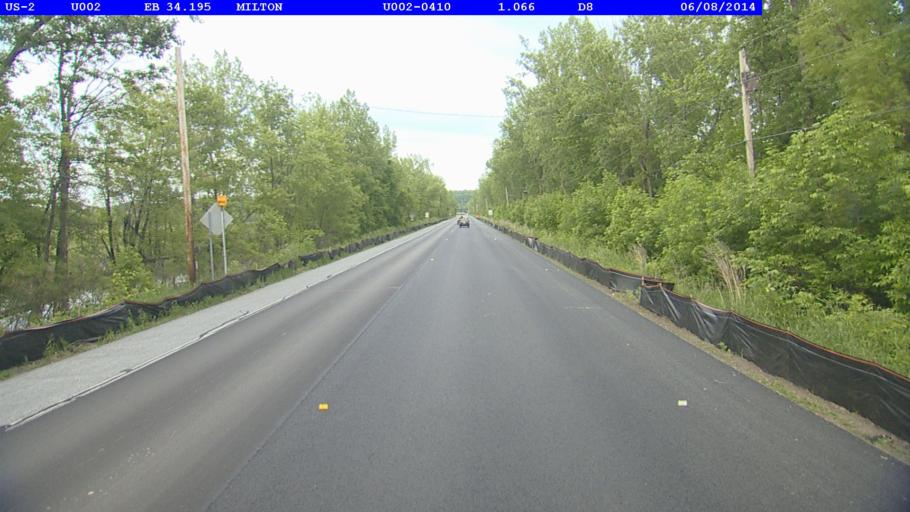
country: US
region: Vermont
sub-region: Chittenden County
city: Colchester
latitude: 44.6252
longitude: -73.2363
